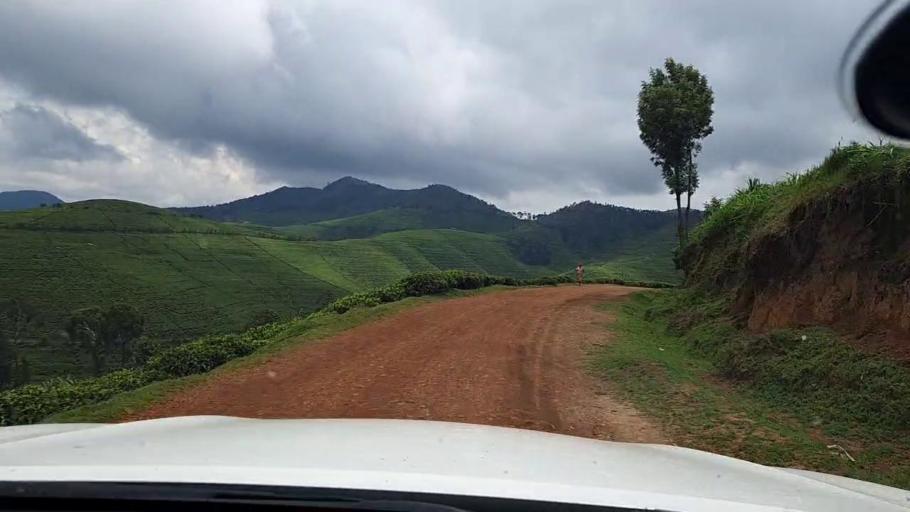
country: RW
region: Western Province
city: Kibuye
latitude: -2.1723
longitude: 29.4369
